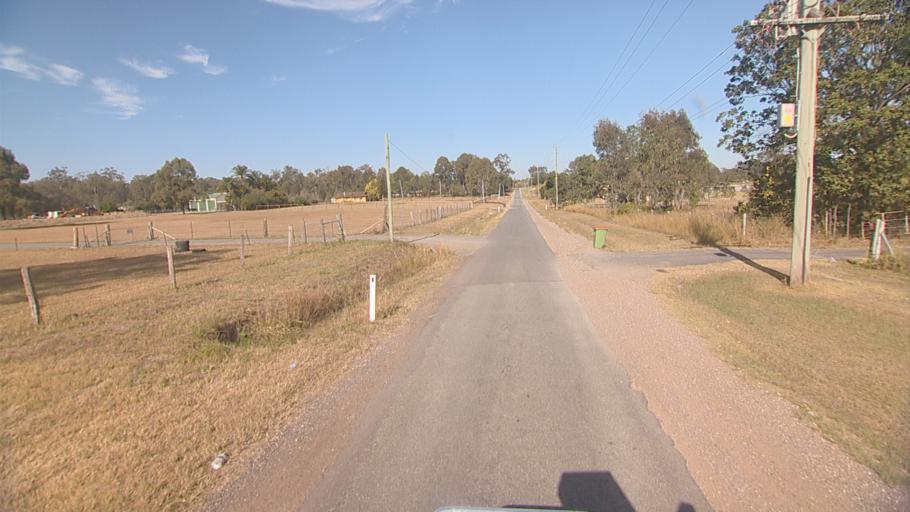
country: AU
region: Queensland
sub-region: Logan
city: North Maclean
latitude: -27.7766
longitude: 153.0083
